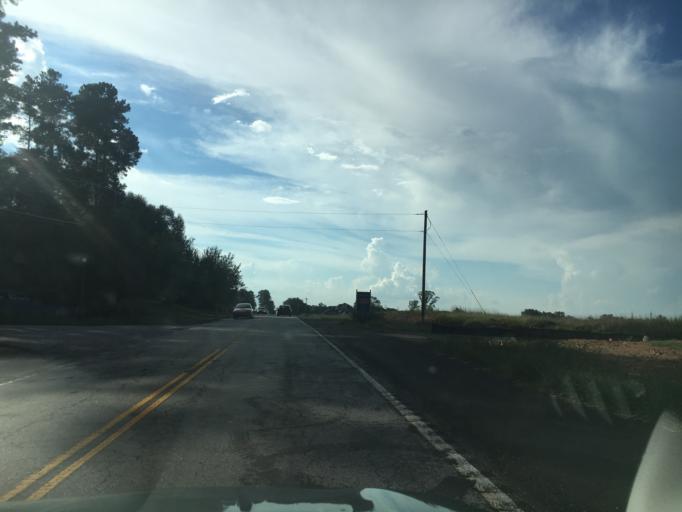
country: US
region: South Carolina
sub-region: Greenville County
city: Five Forks
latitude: 34.8007
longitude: -82.2059
